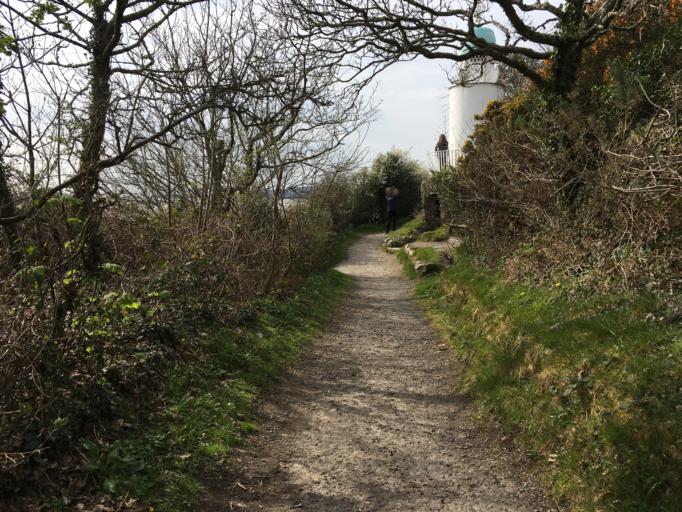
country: GB
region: Wales
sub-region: Gwynedd
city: Porthmadog
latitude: 52.9091
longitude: -4.1033
